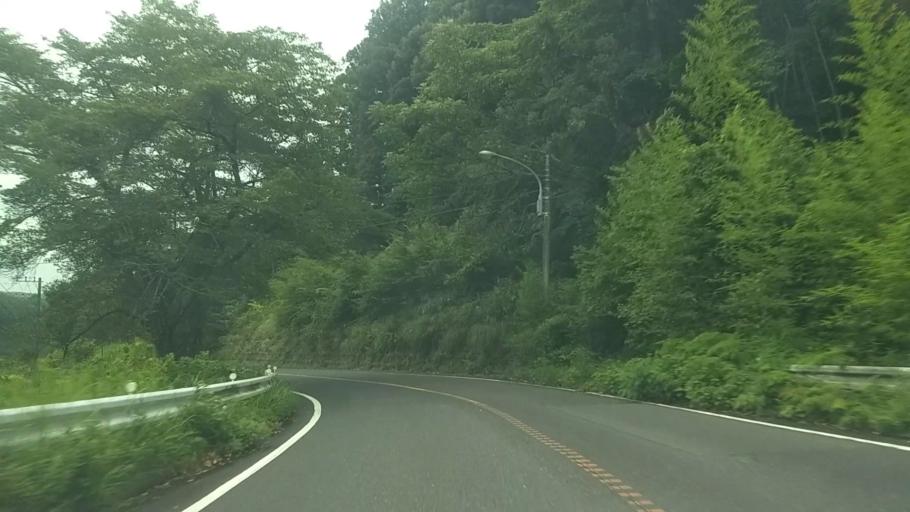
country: JP
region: Chiba
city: Kawaguchi
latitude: 35.2411
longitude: 140.0718
